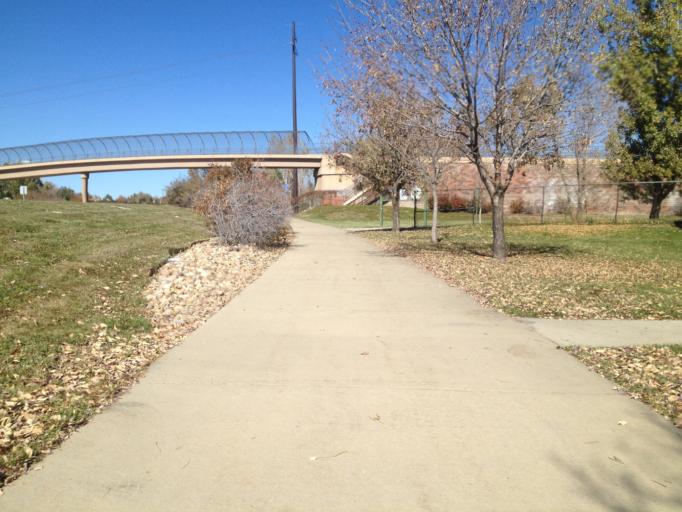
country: US
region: Colorado
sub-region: Boulder County
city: Lafayette
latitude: 39.9897
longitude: -105.0984
